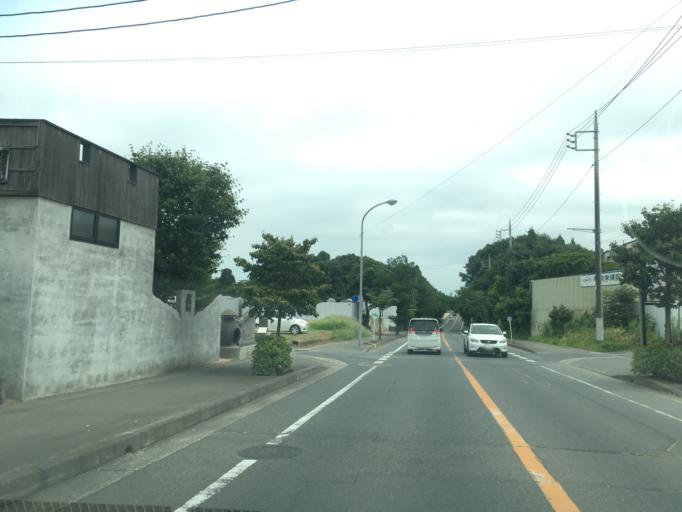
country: JP
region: Ibaraki
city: Katsuta
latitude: 36.3881
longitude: 140.5466
